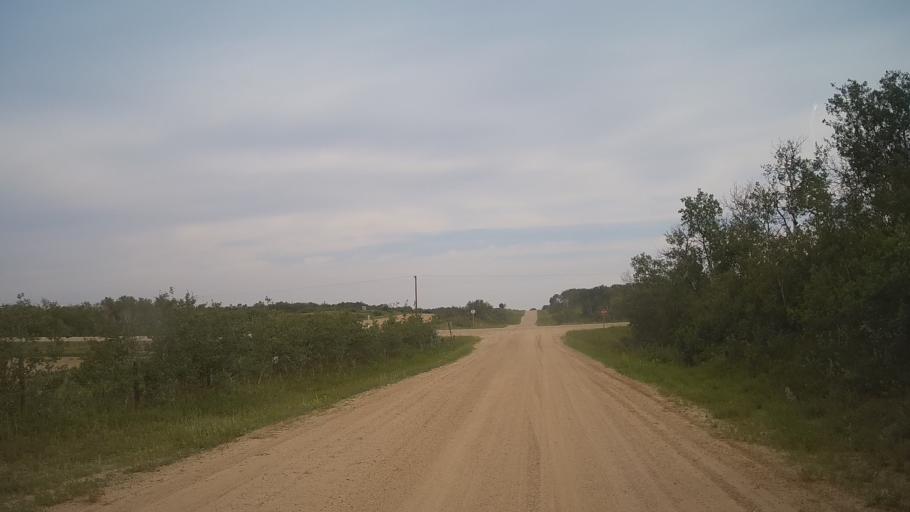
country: CA
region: Saskatchewan
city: Saskatoon
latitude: 51.8523
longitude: -106.5221
